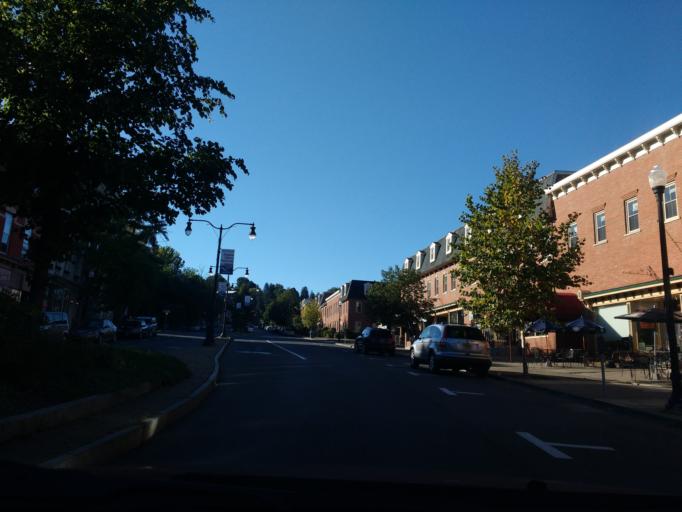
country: US
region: New York
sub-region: Ulster County
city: Port Ewen
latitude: 41.9189
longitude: -73.9831
